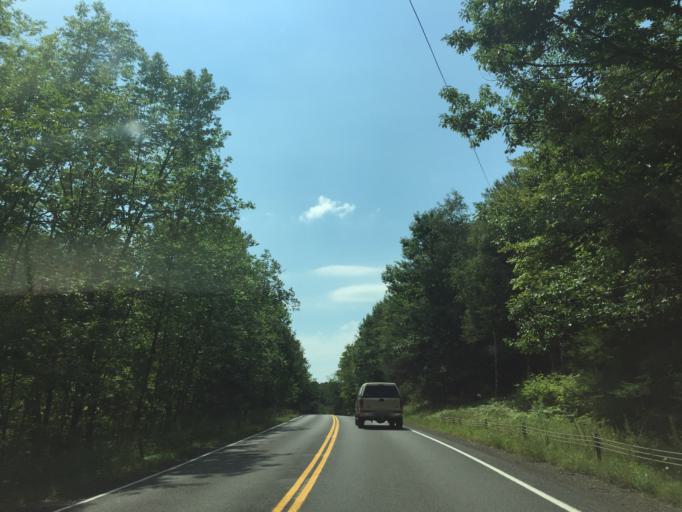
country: US
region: New York
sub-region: Otsego County
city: Cooperstown
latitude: 42.6845
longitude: -74.9005
